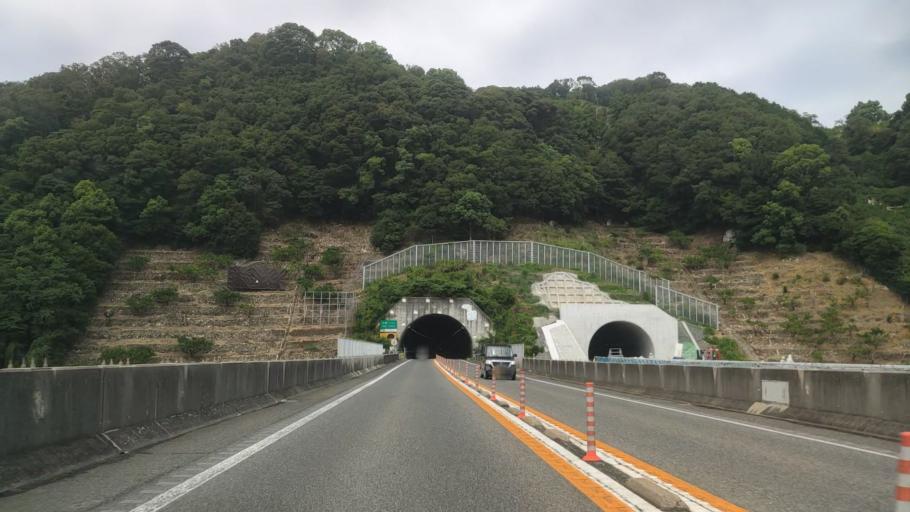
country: JP
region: Wakayama
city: Gobo
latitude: 33.9984
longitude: 135.1962
